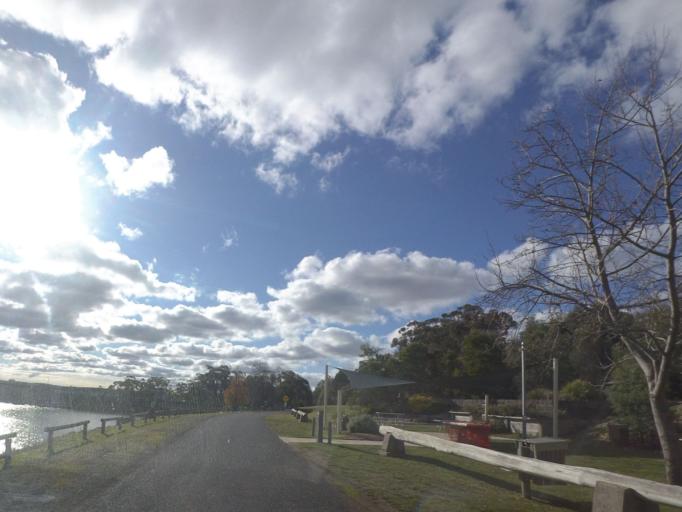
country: AU
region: Victoria
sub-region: Mount Alexander
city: Castlemaine
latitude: -37.2546
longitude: 144.3812
